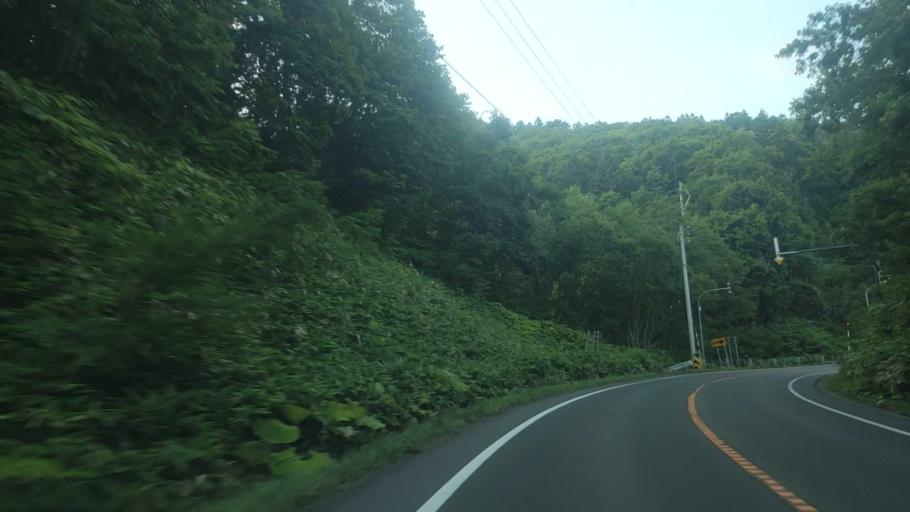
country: JP
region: Hokkaido
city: Bibai
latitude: 43.2677
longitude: 142.0325
